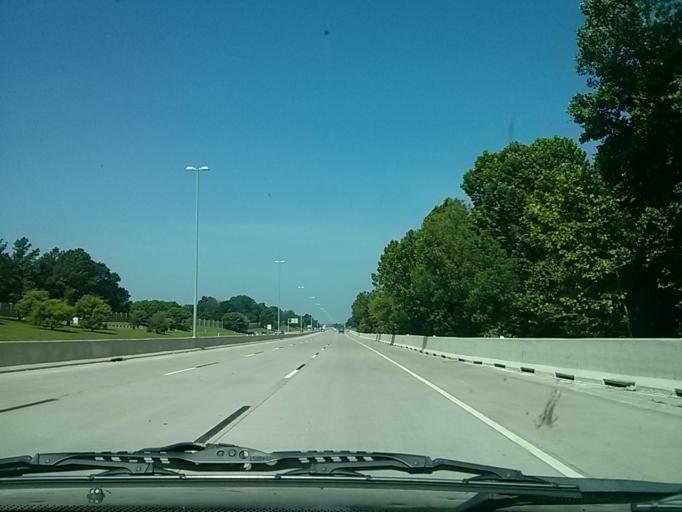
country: US
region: Oklahoma
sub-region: Tulsa County
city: Jenks
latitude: 36.0256
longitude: -95.9229
